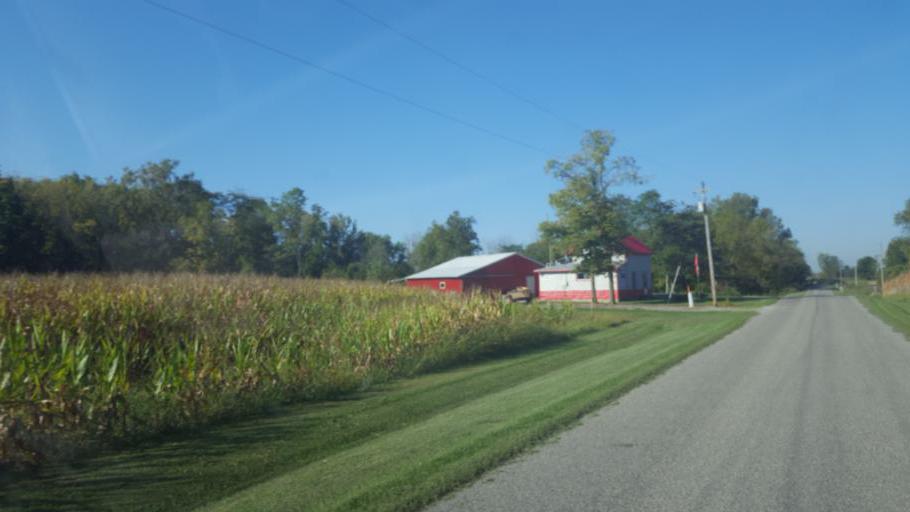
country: US
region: Ohio
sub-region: Union County
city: Richwood
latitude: 40.4960
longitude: -83.4596
